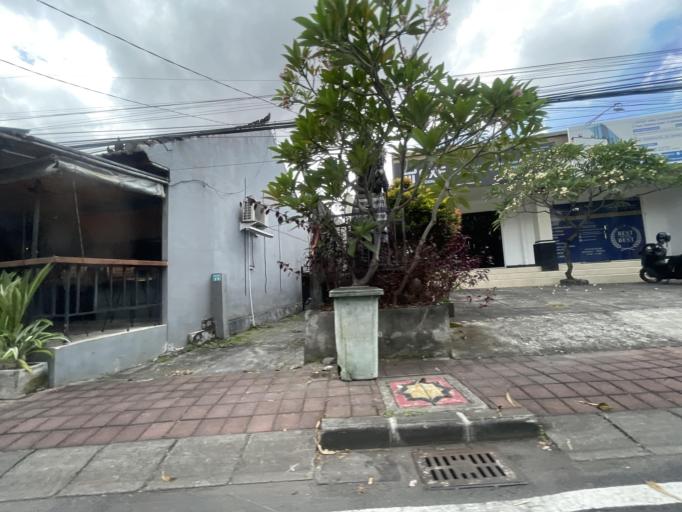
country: ID
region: Bali
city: Kuta
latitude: -8.6903
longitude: 115.1747
